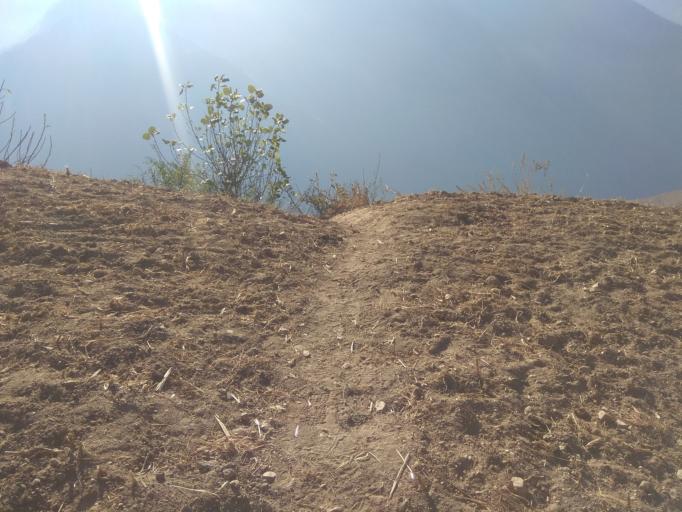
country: NP
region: Mid Western
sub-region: Karnali Zone
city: Jumla
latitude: 29.3136
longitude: 81.7343
